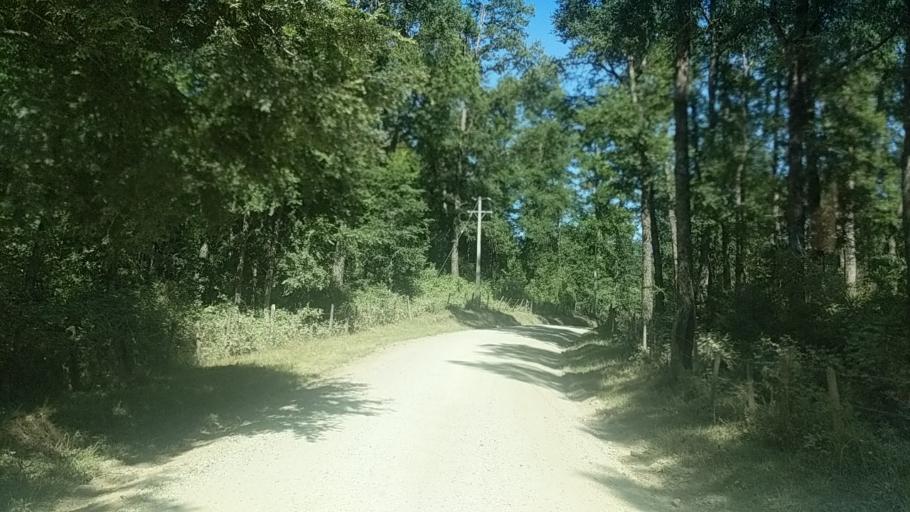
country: CL
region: Araucania
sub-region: Provincia de Cautin
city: Pucon
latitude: -39.0652
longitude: -71.7375
